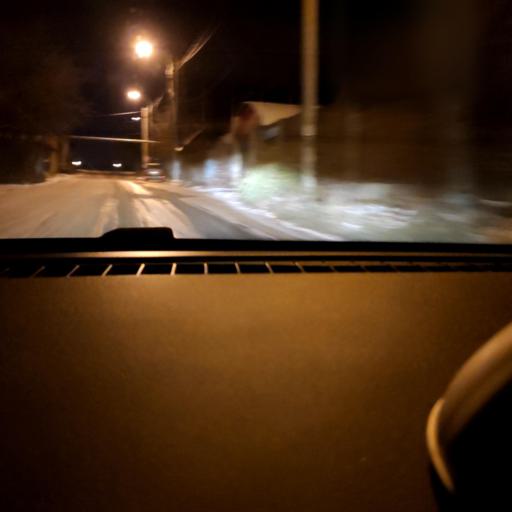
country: RU
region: Samara
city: Petra-Dubrava
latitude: 53.2869
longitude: 50.2429
